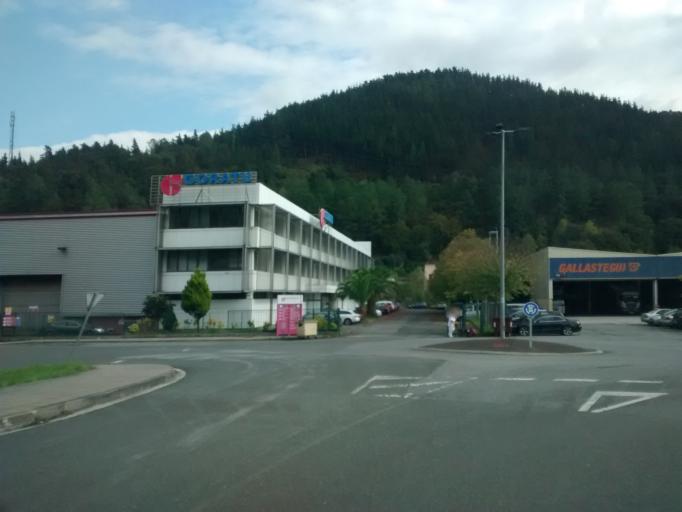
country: ES
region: Basque Country
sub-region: Provincia de Guipuzcoa
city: Elgoibar
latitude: 43.2228
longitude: -2.4063
